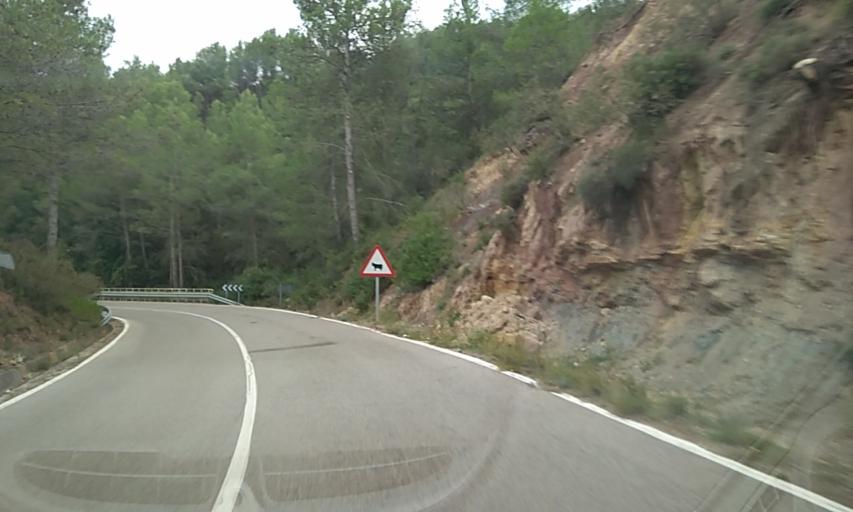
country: ES
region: Valencia
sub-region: Provincia de Castello
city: Puebla de Arenoso
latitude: 40.0883
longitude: -0.5679
